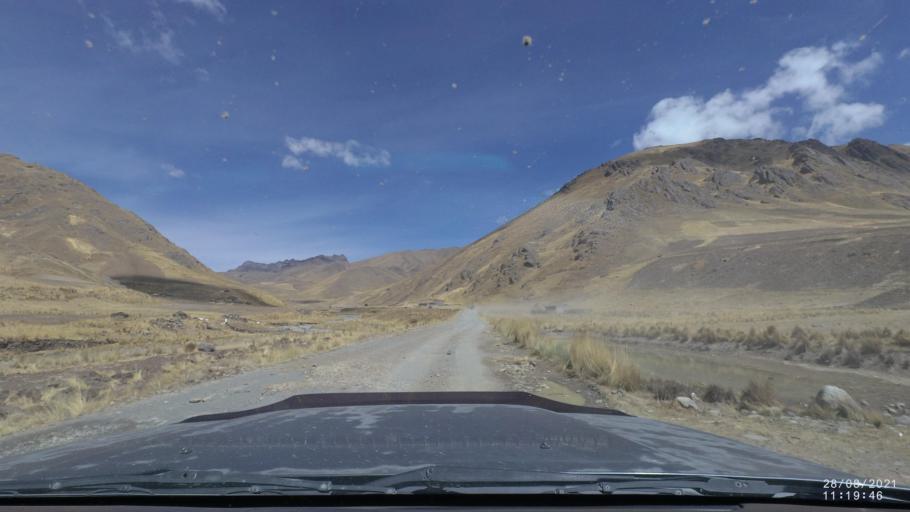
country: BO
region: Cochabamba
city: Cochabamba
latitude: -17.1552
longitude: -66.3354
